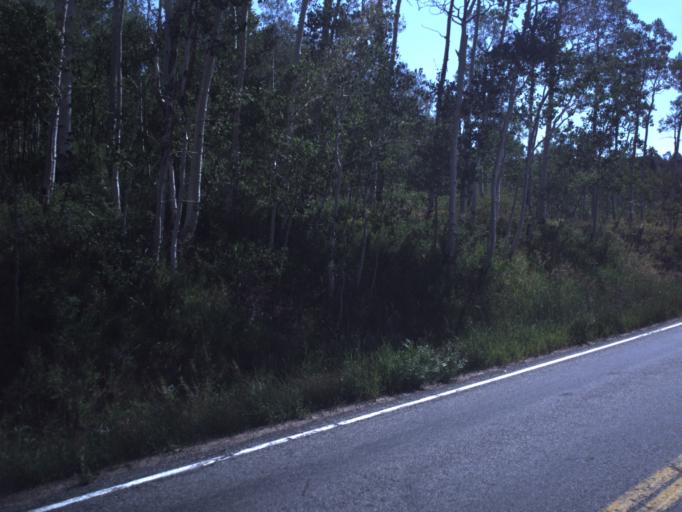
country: US
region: Utah
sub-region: Sanpete County
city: Fairview
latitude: 39.6765
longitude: -111.3228
